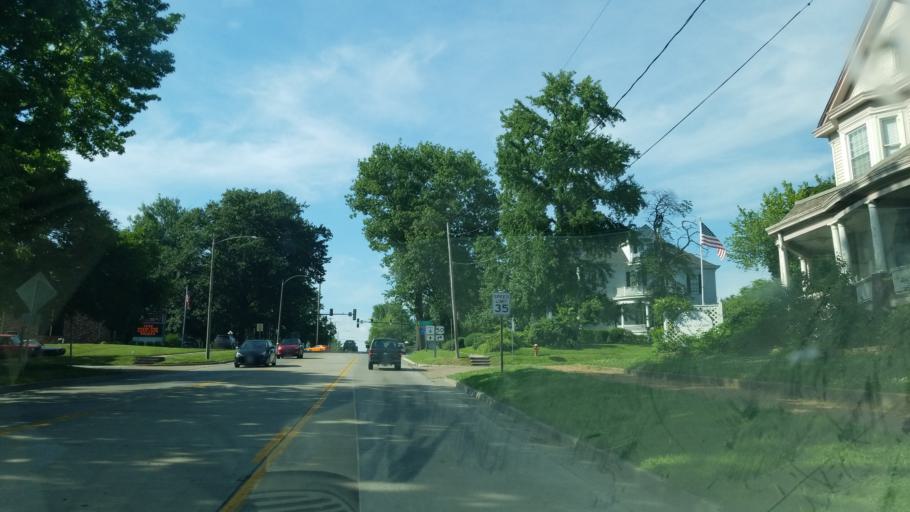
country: US
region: Illinois
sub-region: Saint Clair County
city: Lebanon
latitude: 38.6026
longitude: -89.8076
